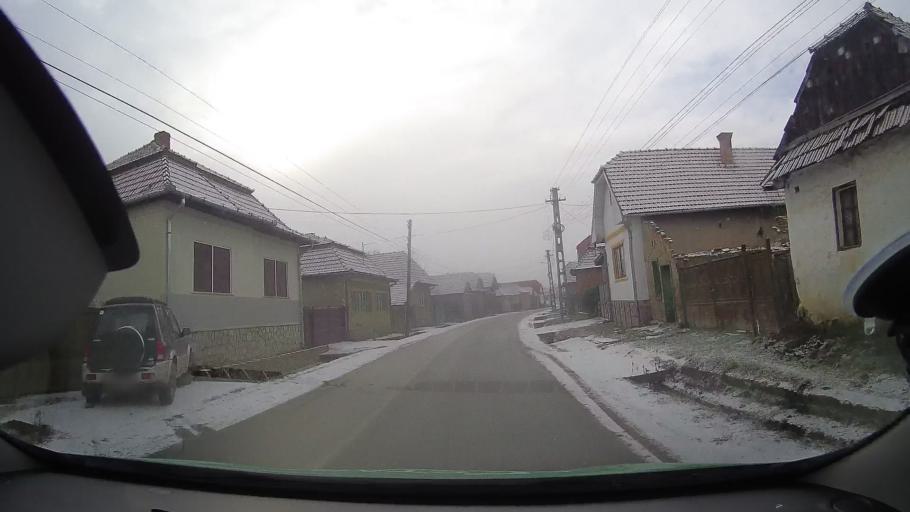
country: RO
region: Alba
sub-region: Comuna Rimetea
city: Rimetea
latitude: 46.4216
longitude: 23.5610
